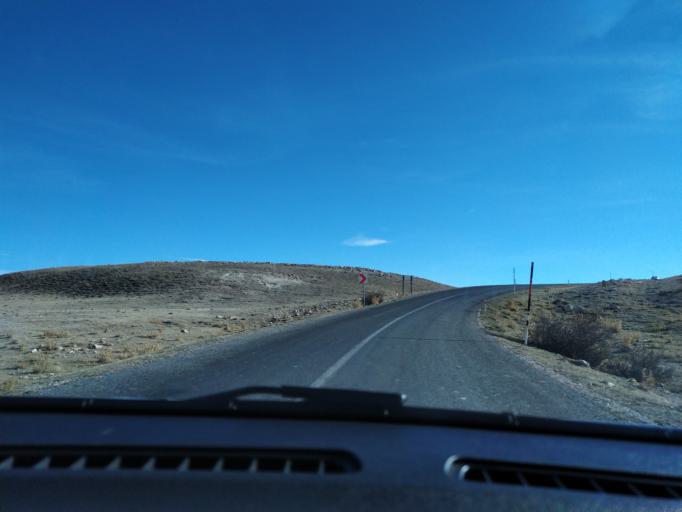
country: TR
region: Kayseri
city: Orensehir
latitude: 38.9778
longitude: 36.6732
